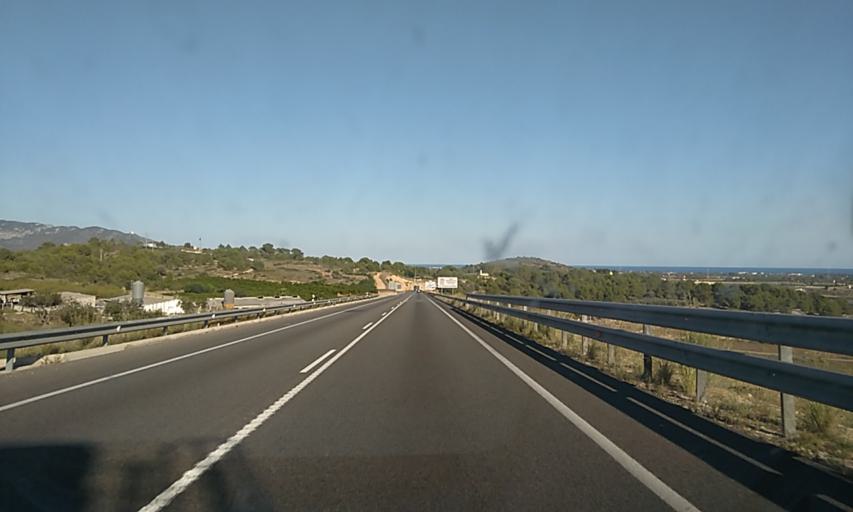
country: ES
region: Valencia
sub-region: Provincia de Castello
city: Torreblanca
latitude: 40.2314
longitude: 0.2002
